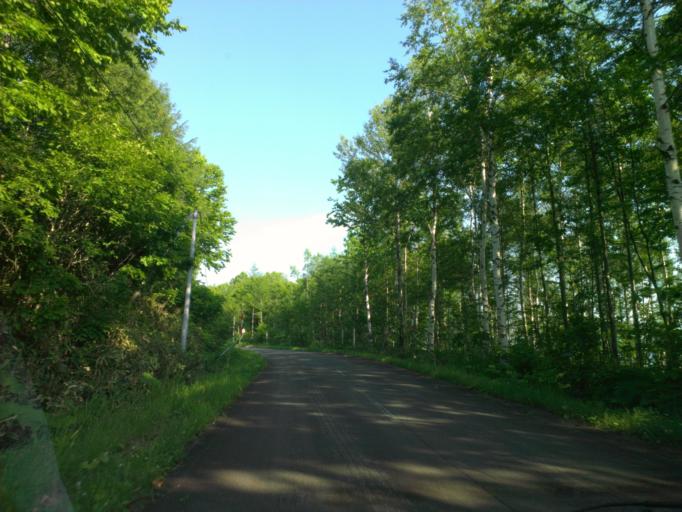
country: JP
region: Hokkaido
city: Shimo-furano
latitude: 43.5110
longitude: 142.6295
